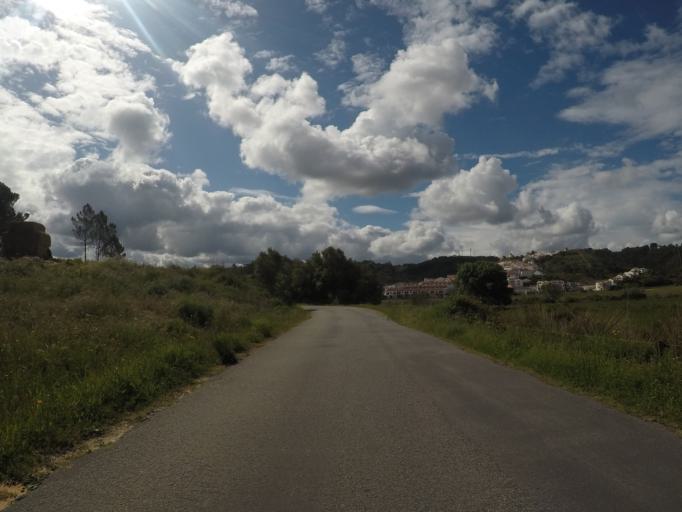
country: PT
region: Beja
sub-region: Odemira
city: Sao Teotonio
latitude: 37.4374
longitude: -8.7725
